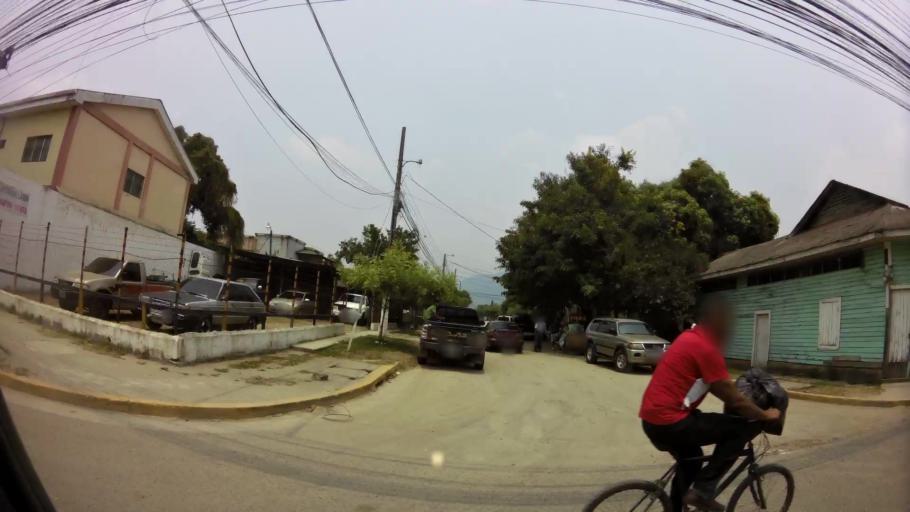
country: HN
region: Yoro
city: El Progreso
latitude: 15.3966
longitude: -87.8086
